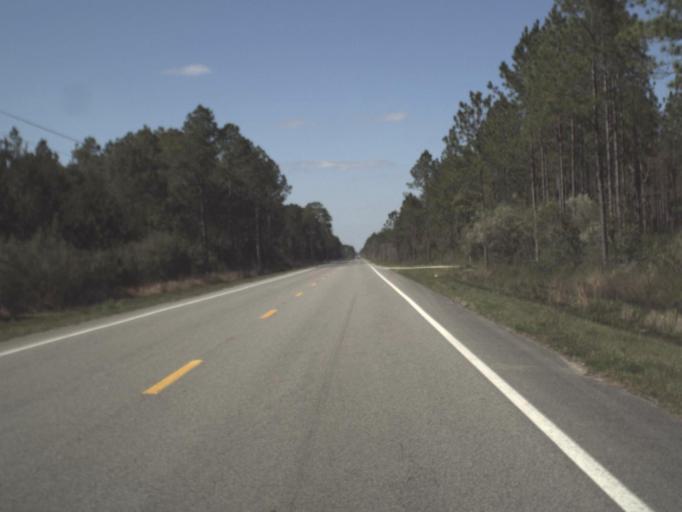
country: US
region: Florida
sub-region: Gulf County
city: Wewahitchka
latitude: 29.9889
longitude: -85.1690
